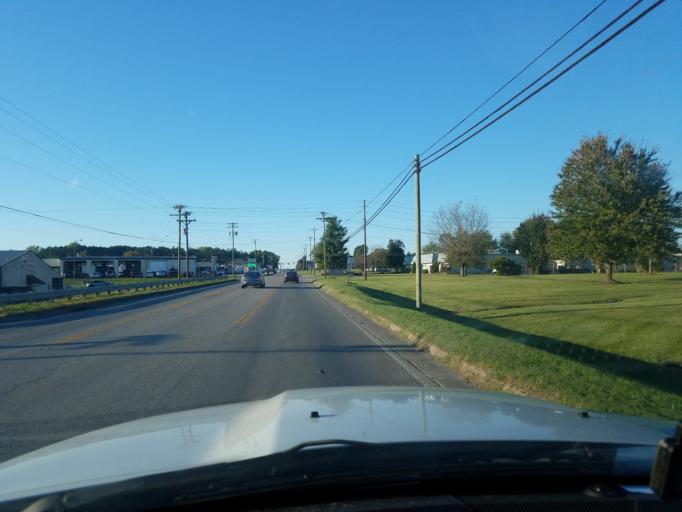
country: US
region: Kentucky
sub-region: Laurel County
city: London
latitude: 37.0917
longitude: -84.0644
